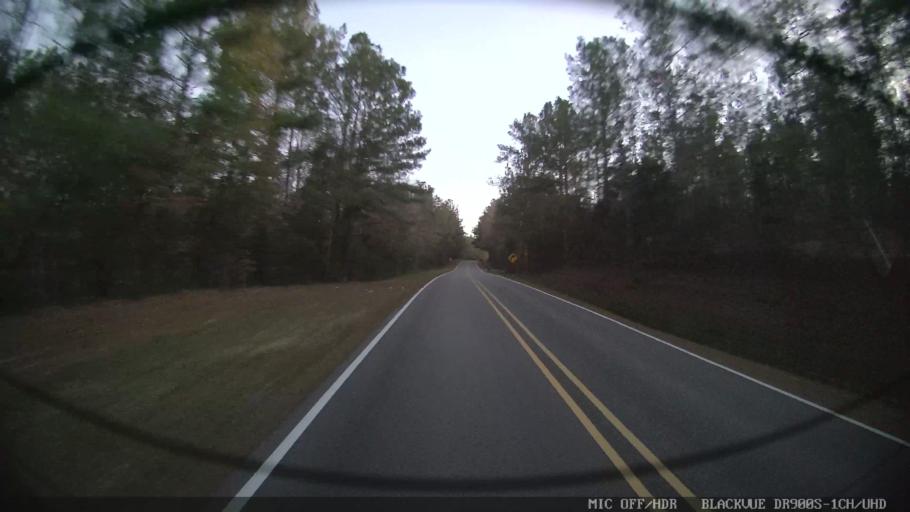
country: US
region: Mississippi
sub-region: Perry County
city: New Augusta
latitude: 31.0783
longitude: -89.1865
